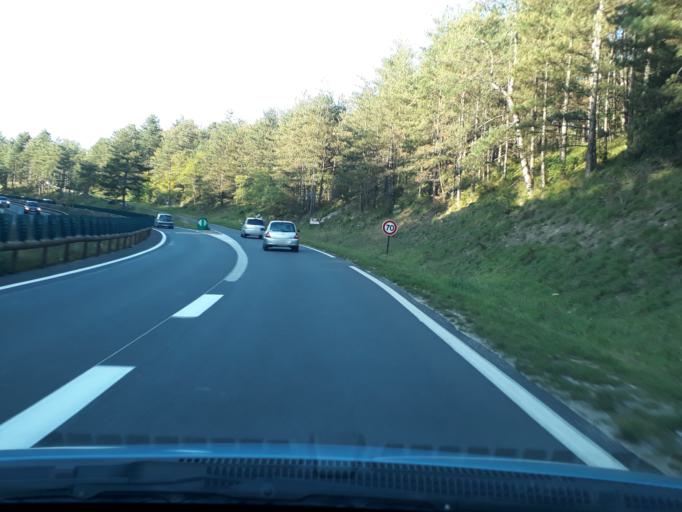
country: FR
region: Ile-de-France
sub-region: Departement de Seine-et-Marne
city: Avon
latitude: 48.4228
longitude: 2.7104
